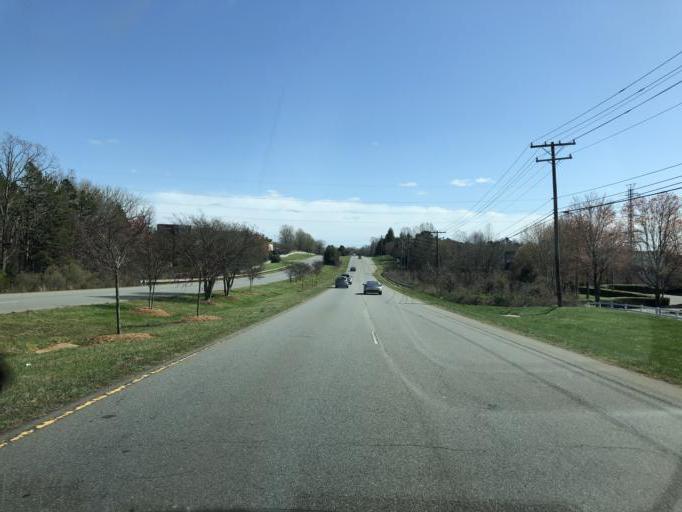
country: US
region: North Carolina
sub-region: Mecklenburg County
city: Huntersville
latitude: 35.3431
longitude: -80.8377
